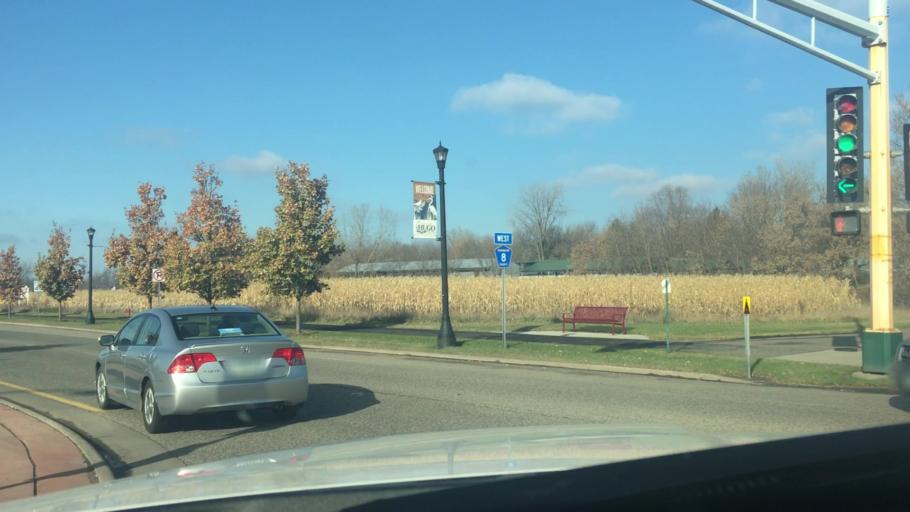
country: US
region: Minnesota
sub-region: Washington County
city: Hugo
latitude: 45.1572
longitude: -92.9942
